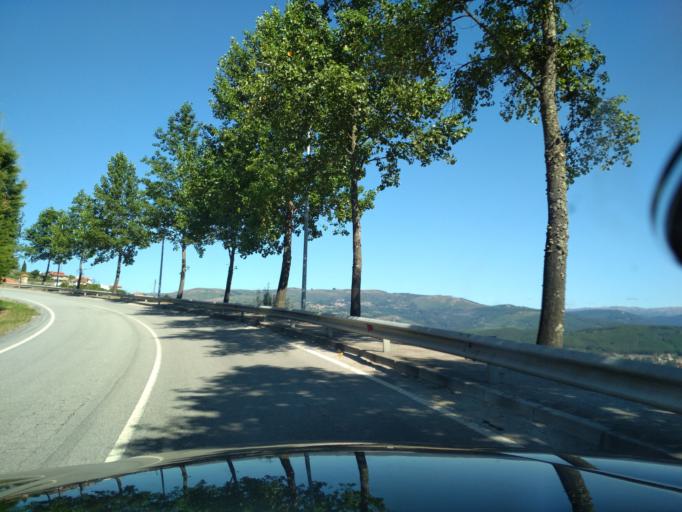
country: PT
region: Vila Real
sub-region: Ribeira de Pena
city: Ribeira de Pena
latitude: 41.5187
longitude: -7.8007
